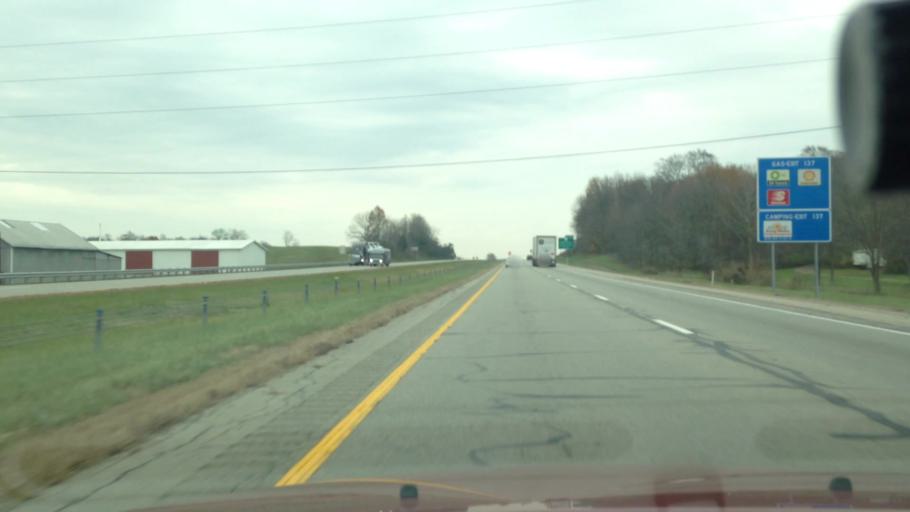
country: US
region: Indiana
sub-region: Wayne County
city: Cambridge City
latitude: 39.8532
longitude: -85.1641
